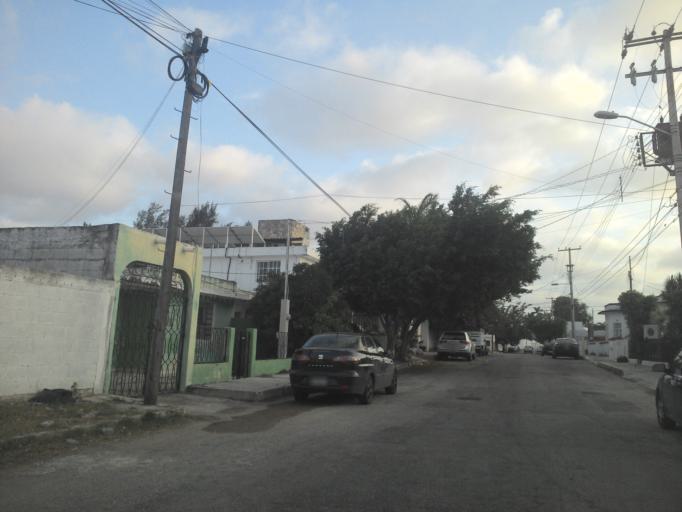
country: MX
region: Yucatan
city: Merida
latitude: 20.9966
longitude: -89.6153
